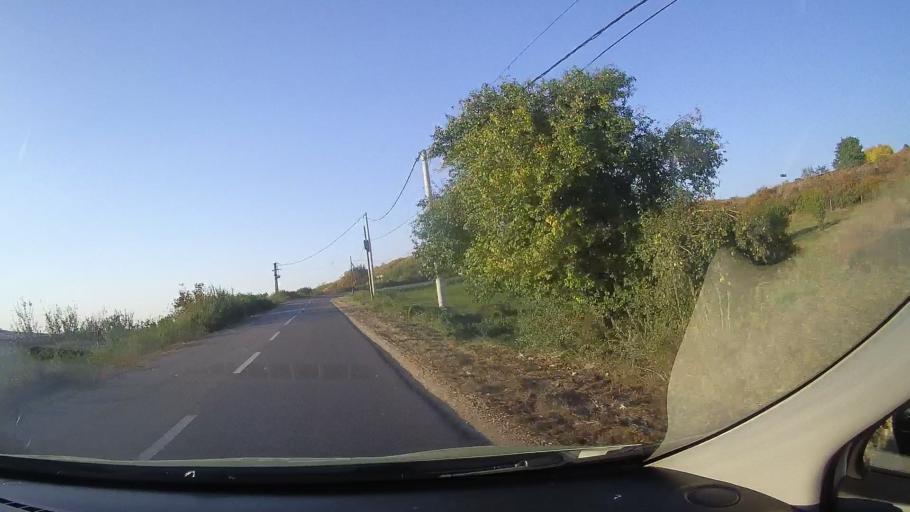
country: RO
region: Bihor
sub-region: Comuna Biharea
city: Oradea
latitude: 47.0959
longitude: 21.9233
